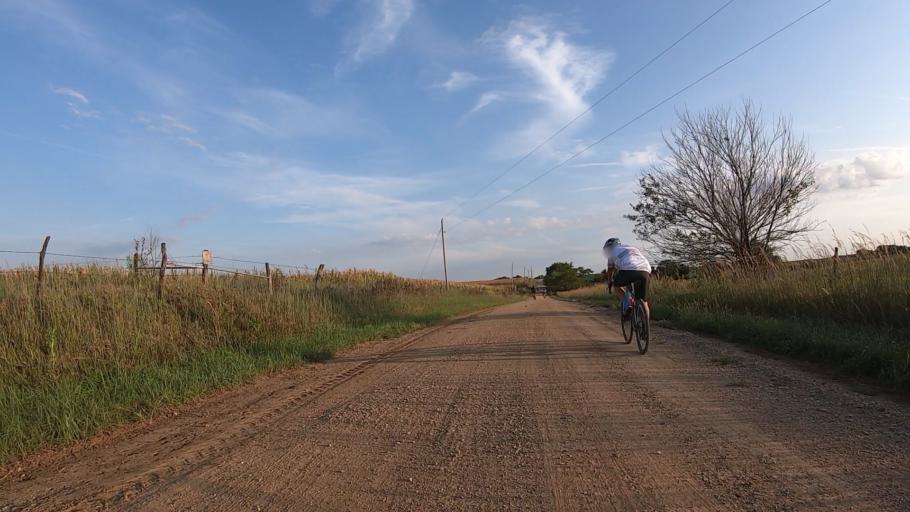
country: US
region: Kansas
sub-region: Marshall County
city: Blue Rapids
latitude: 39.7657
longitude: -96.7130
